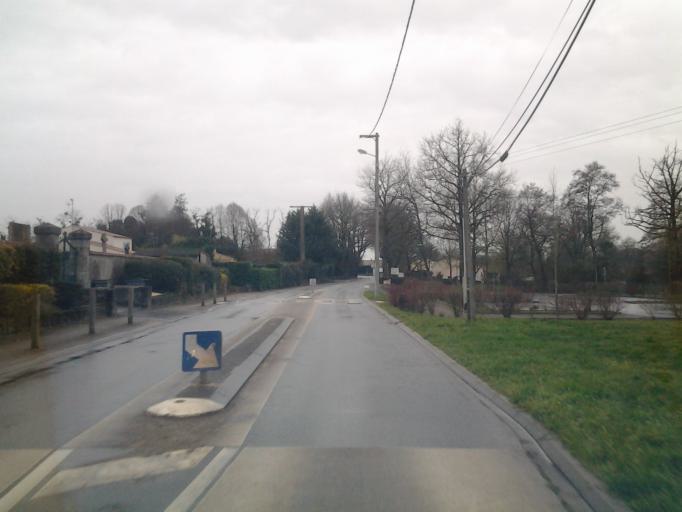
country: FR
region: Pays de la Loire
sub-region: Departement de la Vendee
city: Landeronde
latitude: 46.6612
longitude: -1.5716
